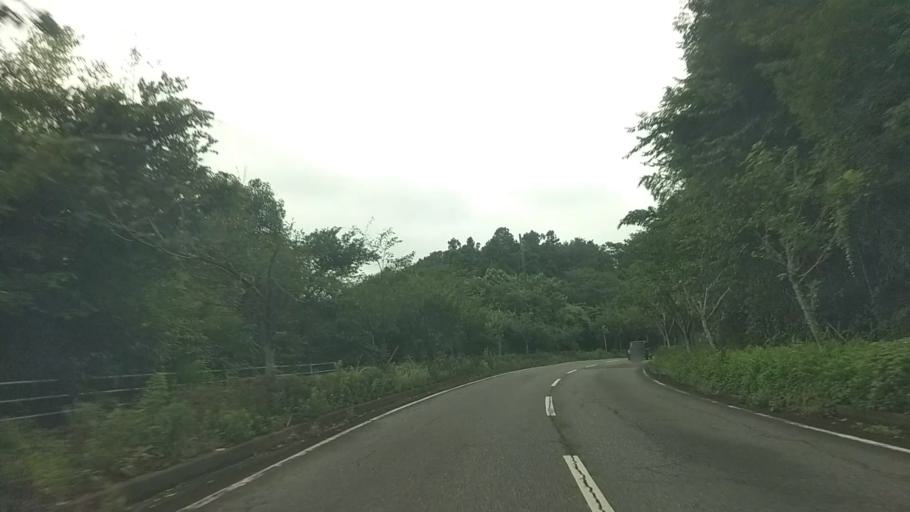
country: JP
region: Chiba
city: Kisarazu
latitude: 35.3826
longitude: 140.0076
